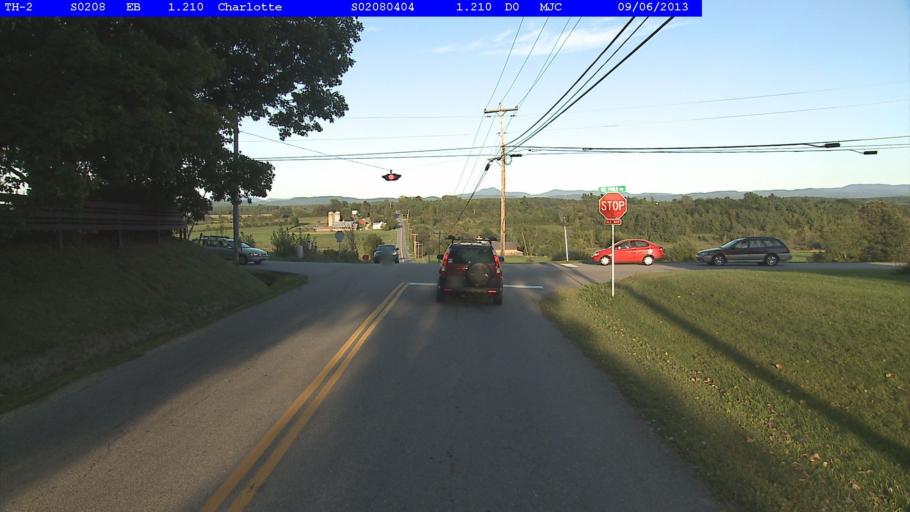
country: US
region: Vermont
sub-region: Chittenden County
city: Hinesburg
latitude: 44.3156
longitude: -73.2241
